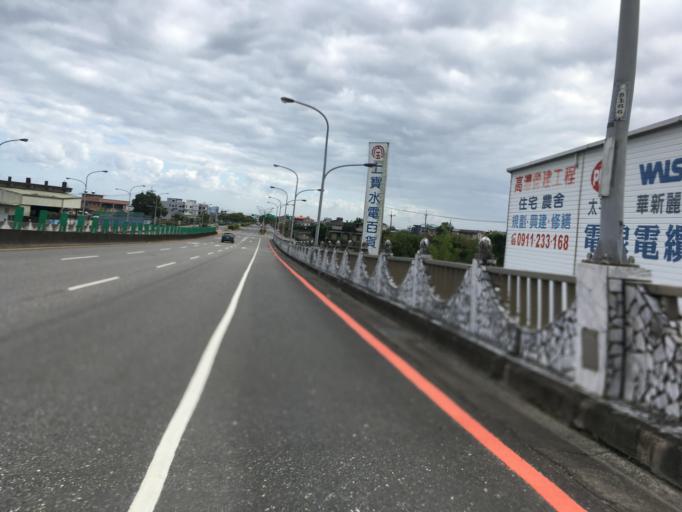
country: TW
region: Taiwan
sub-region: Yilan
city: Yilan
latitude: 24.7746
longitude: 121.7632
